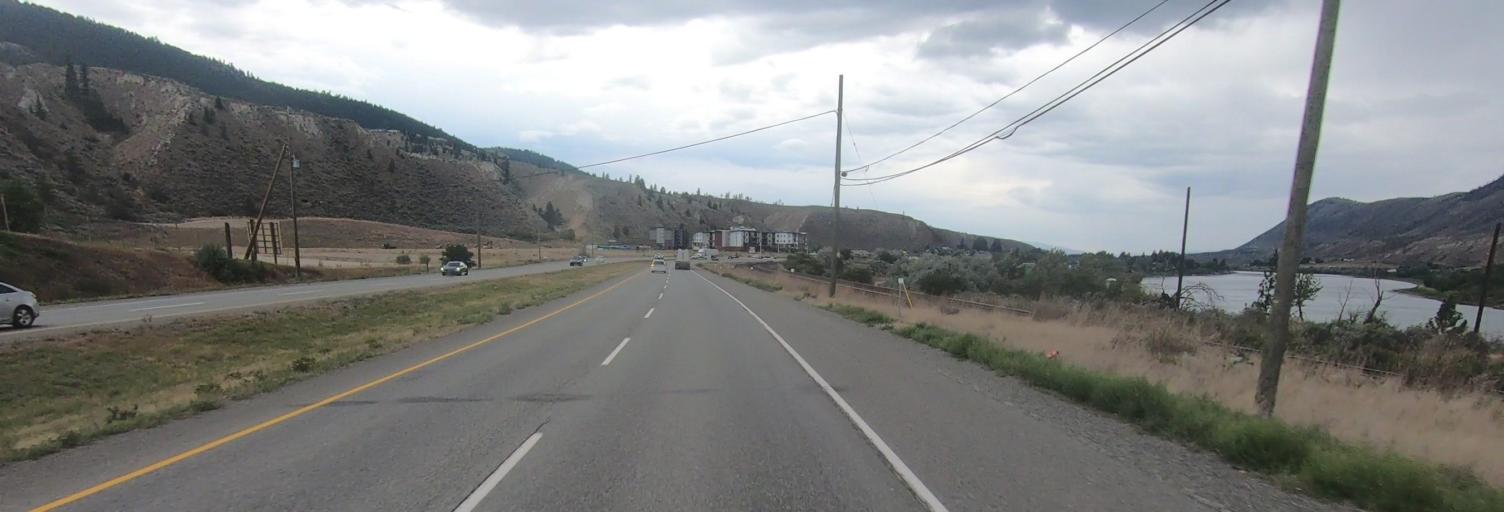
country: CA
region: British Columbia
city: Kamloops
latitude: 50.6720
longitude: -120.2161
